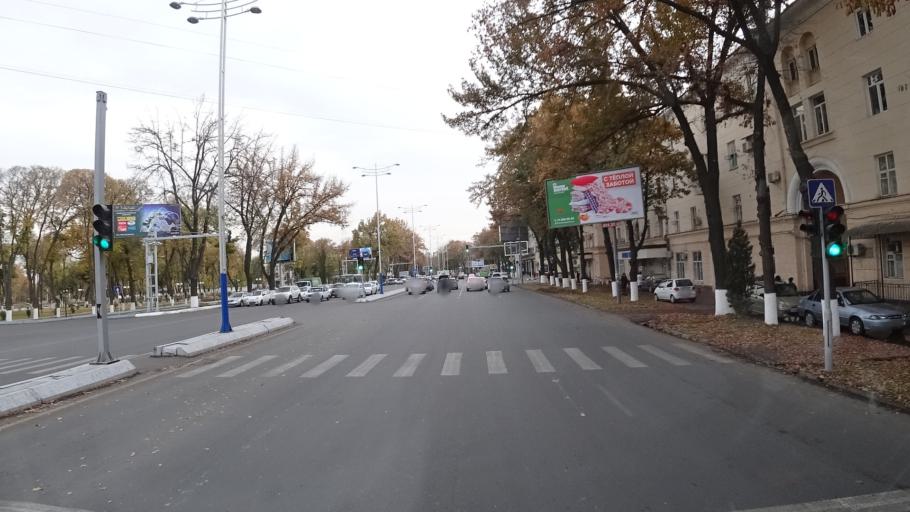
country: UZ
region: Toshkent Shahri
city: Tashkent
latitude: 41.2942
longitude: 69.2506
